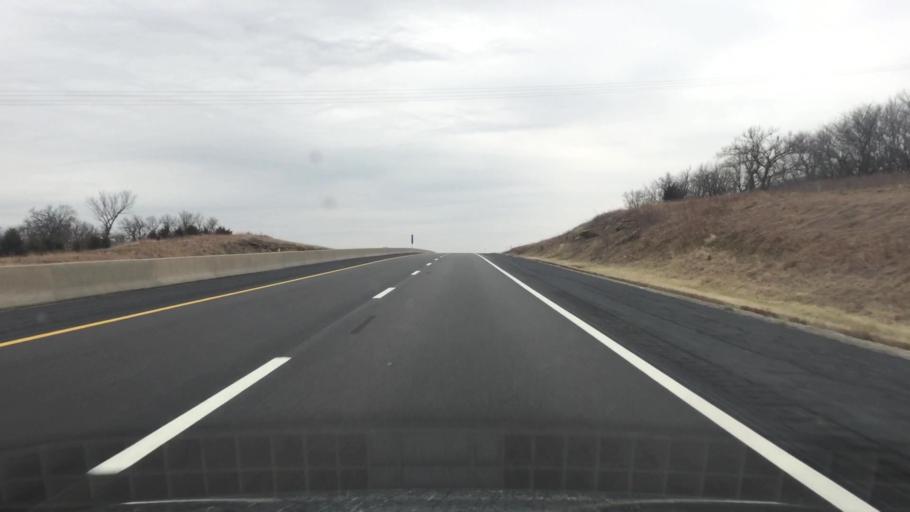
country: US
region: Kansas
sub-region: Shawnee County
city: Auburn
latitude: 38.7831
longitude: -95.9170
